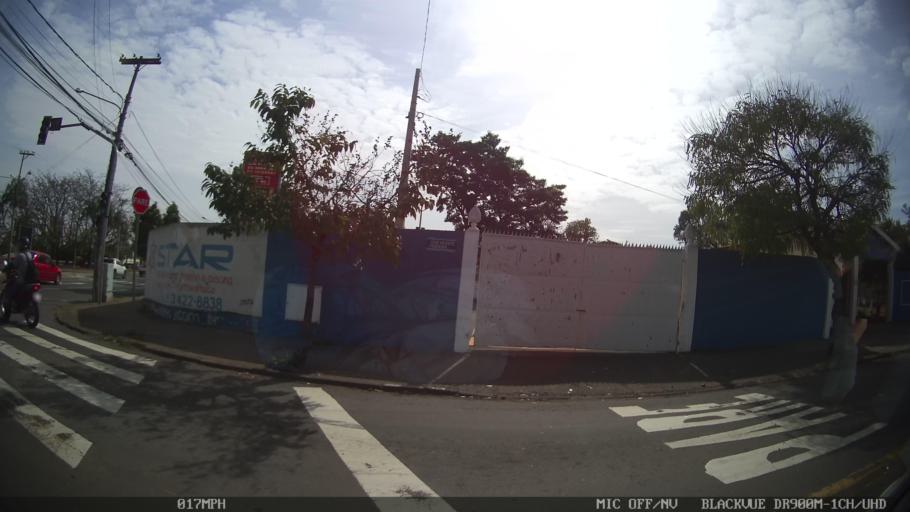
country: BR
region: Sao Paulo
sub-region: Piracicaba
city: Piracicaba
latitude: -22.7461
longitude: -47.6387
